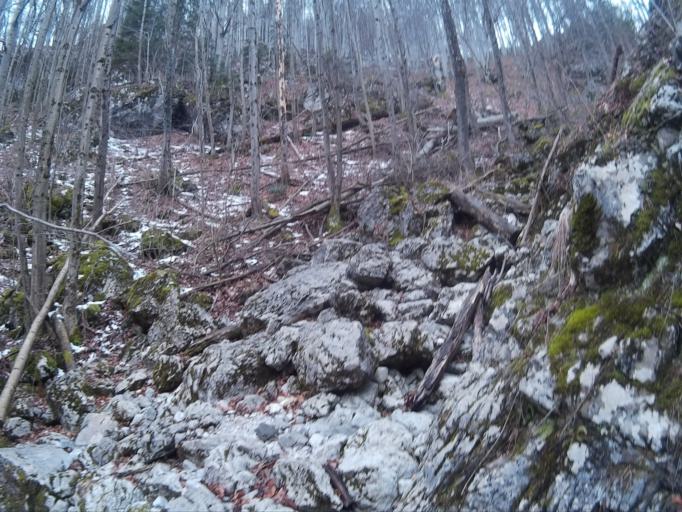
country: AT
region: Lower Austria
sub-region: Politischer Bezirk Neunkirchen
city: Schwarzau im Gebirge
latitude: 47.7512
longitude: 15.7707
